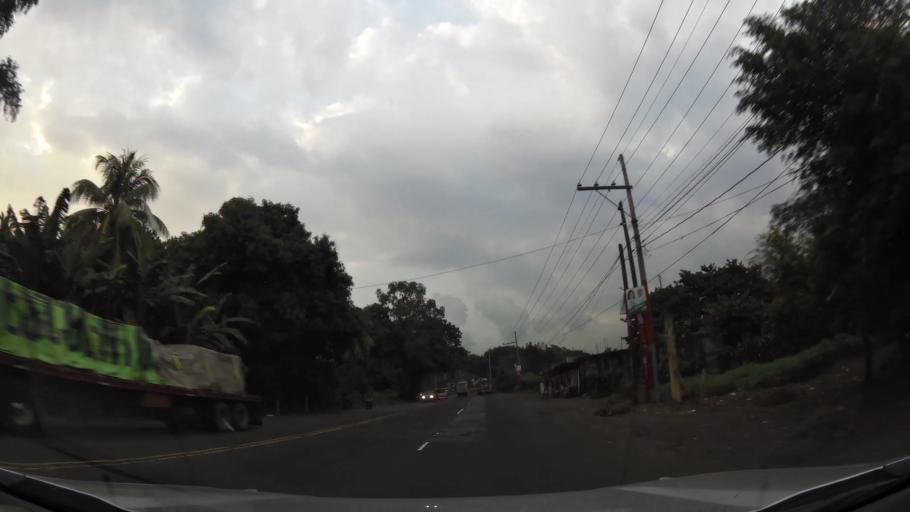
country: GT
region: Escuintla
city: Siquinala
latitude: 14.2914
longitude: -90.9410
